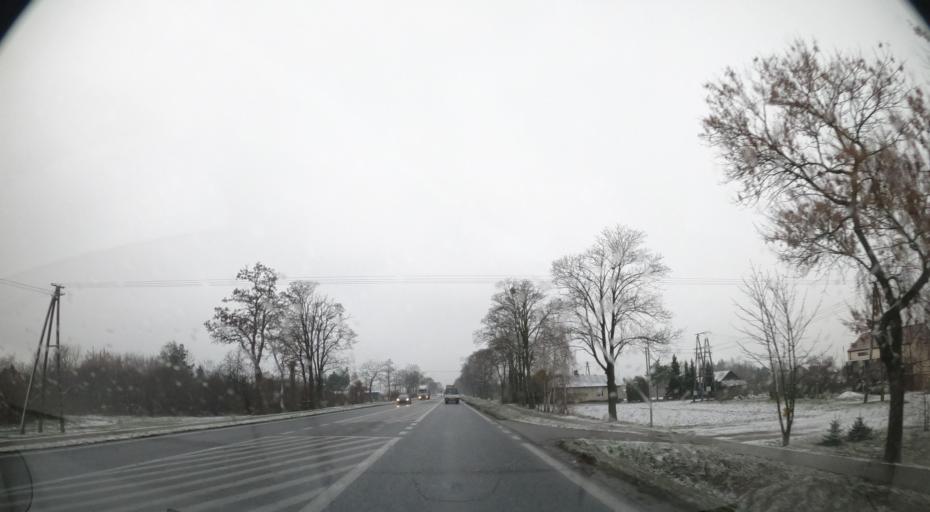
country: PL
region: Masovian Voivodeship
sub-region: Powiat sochaczewski
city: Paprotnia
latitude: 52.2134
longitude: 20.4140
